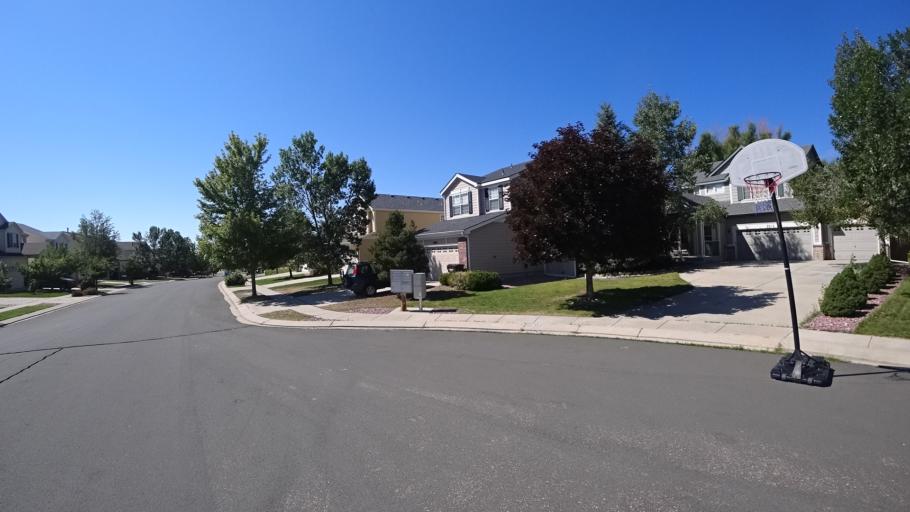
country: US
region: Colorado
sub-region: El Paso County
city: Black Forest
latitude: 38.9454
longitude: -104.7449
